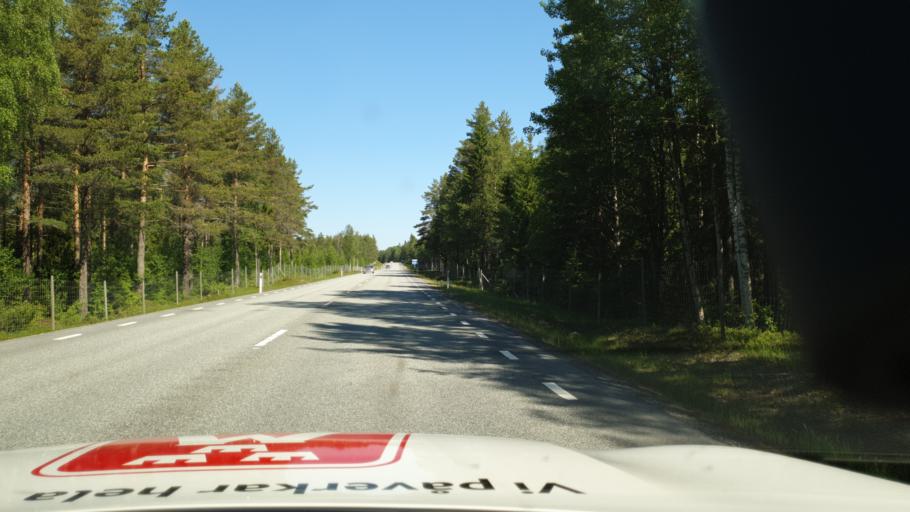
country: SE
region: Vaesterbotten
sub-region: Skelleftea Kommun
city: Burea
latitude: 64.5289
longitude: 21.2581
